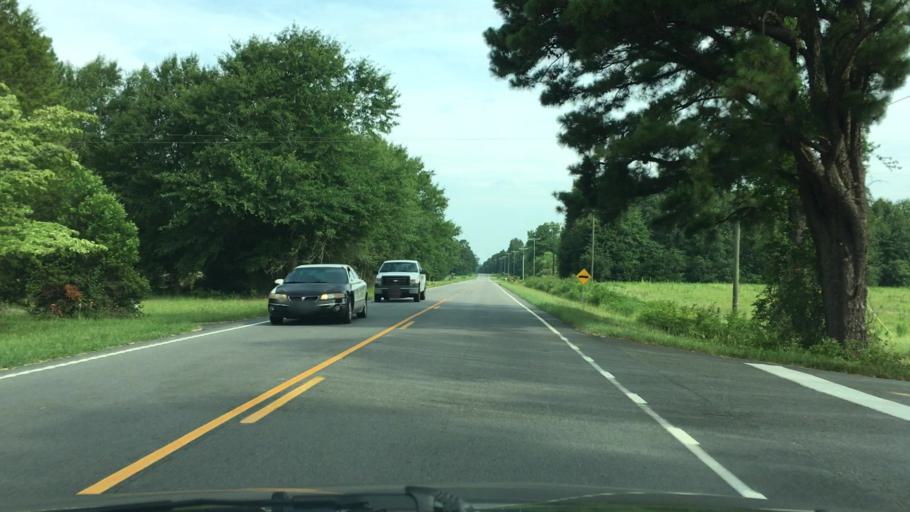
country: US
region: South Carolina
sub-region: Lexington County
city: Batesburg-Leesville
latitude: 33.7158
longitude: -81.4990
